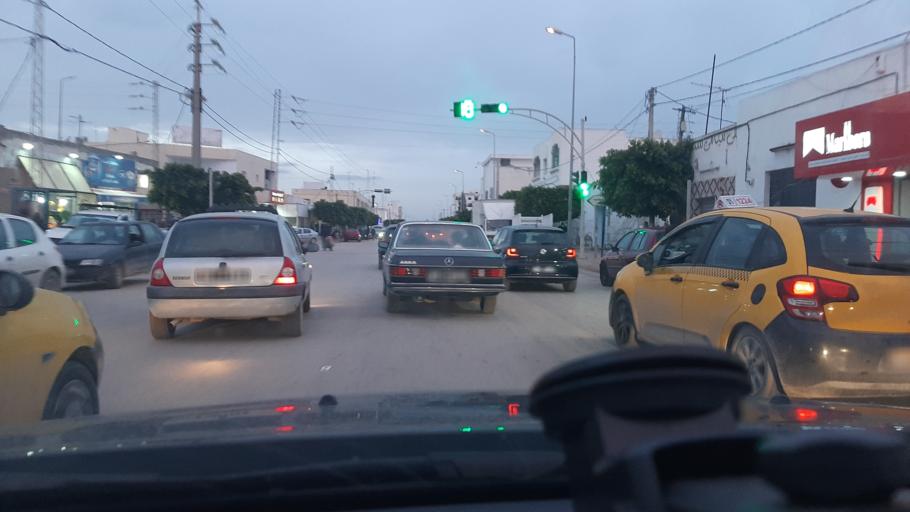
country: TN
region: Safaqis
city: Sfax
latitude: 34.7697
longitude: 10.7066
